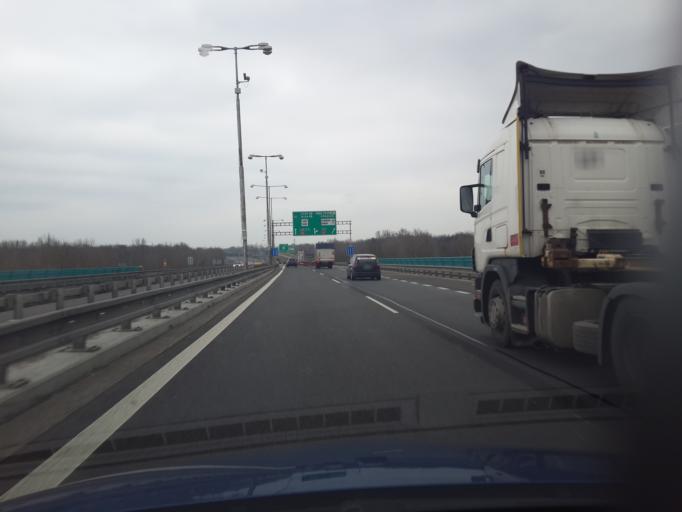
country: SK
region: Bratislavsky
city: Bratislava
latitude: 48.1386
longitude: 17.0746
